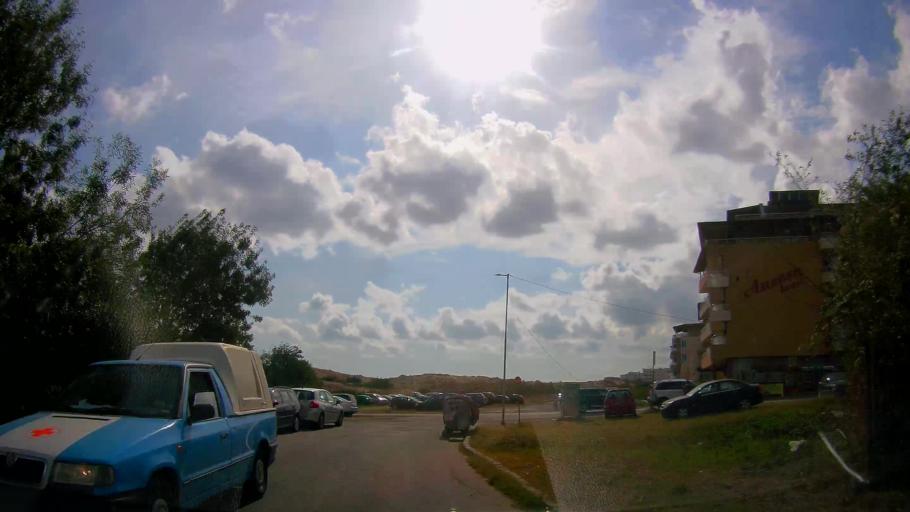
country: BG
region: Burgas
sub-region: Obshtina Primorsko
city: Primorsko
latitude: 42.2714
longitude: 27.7510
